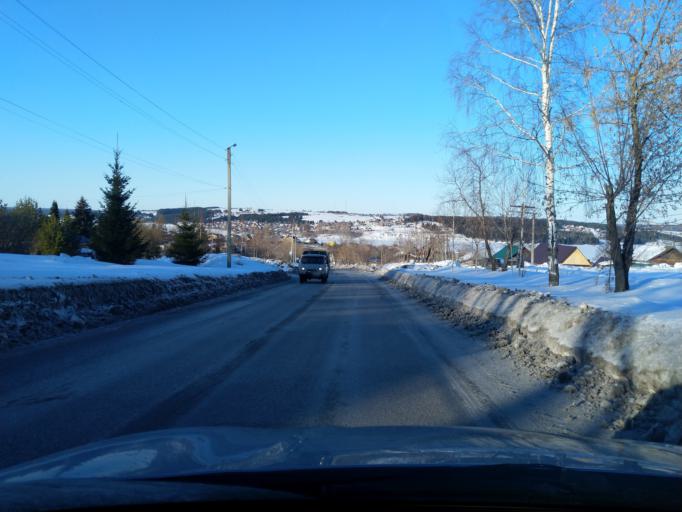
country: RU
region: Perm
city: Polazna
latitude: 58.2923
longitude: 56.4150
